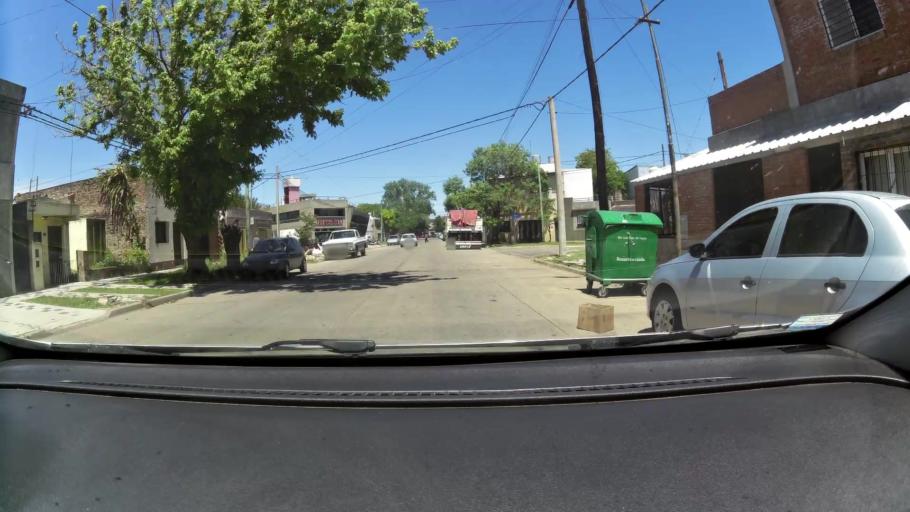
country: AR
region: Santa Fe
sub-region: Departamento de Rosario
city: Rosario
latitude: -32.9449
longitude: -60.7109
